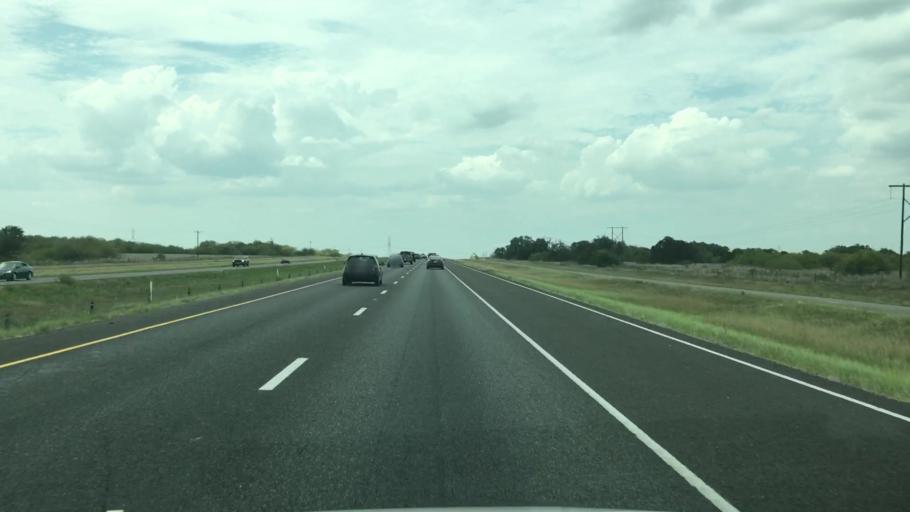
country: US
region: Texas
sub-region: Atascosa County
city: Pleasanton
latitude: 28.8123
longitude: -98.3531
